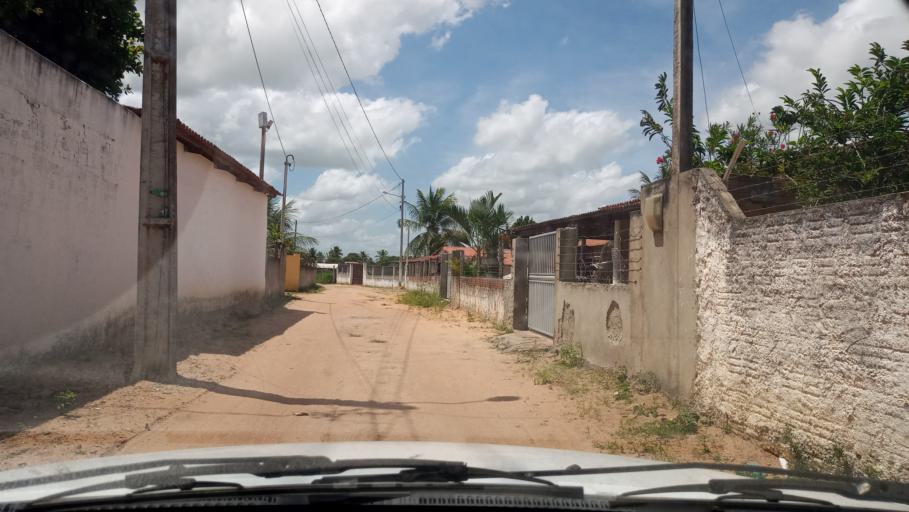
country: BR
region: Rio Grande do Norte
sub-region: Brejinho
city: Brejinho
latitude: -6.2639
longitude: -35.3709
